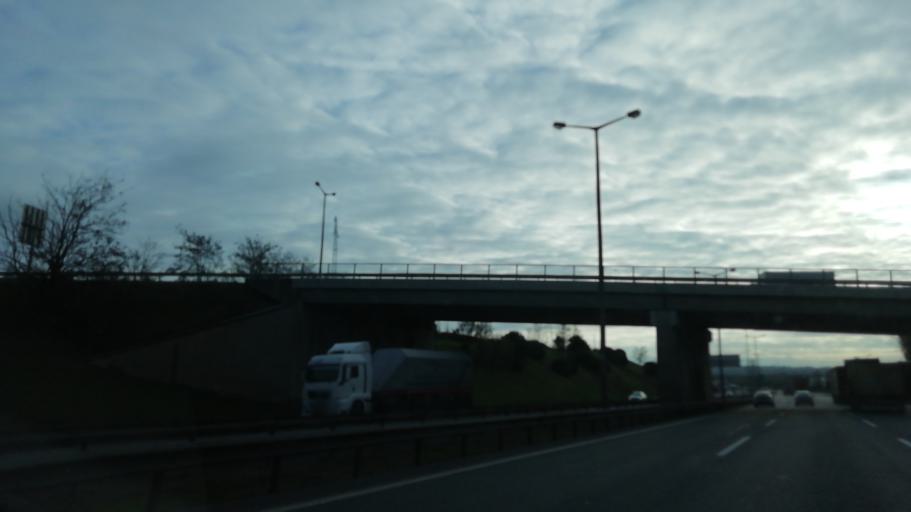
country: TR
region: Istanbul
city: Sultanbeyli
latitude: 40.9365
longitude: 29.3314
